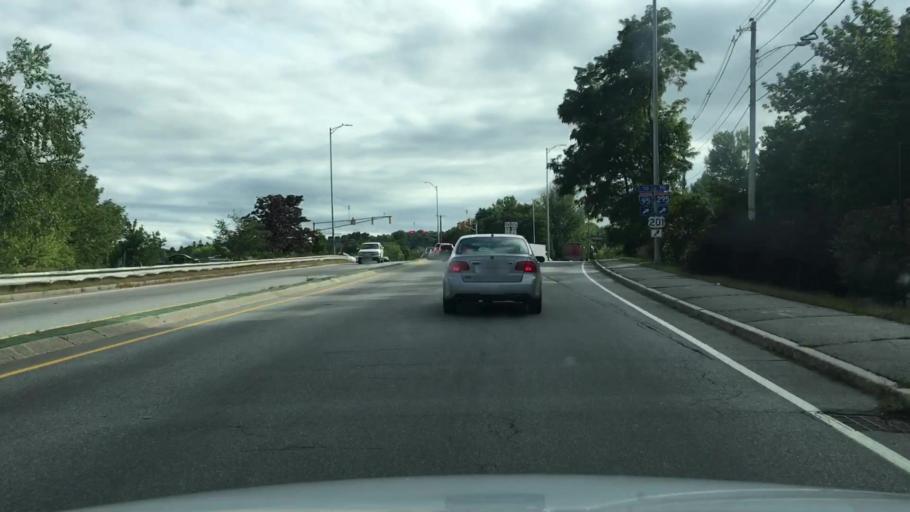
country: US
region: Maine
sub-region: Kennebec County
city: Gardiner
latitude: 44.2347
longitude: -69.7722
